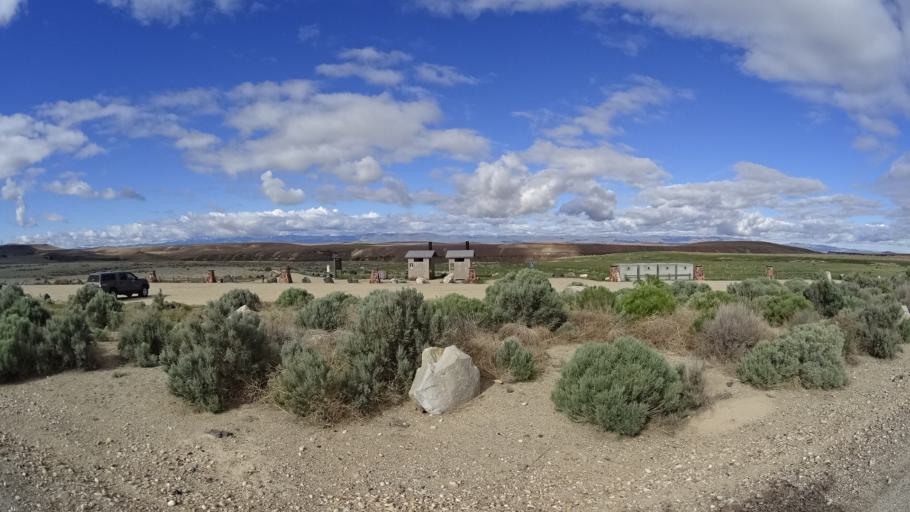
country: US
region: Idaho
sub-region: Owyhee County
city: Murphy
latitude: 43.2765
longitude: -116.3940
